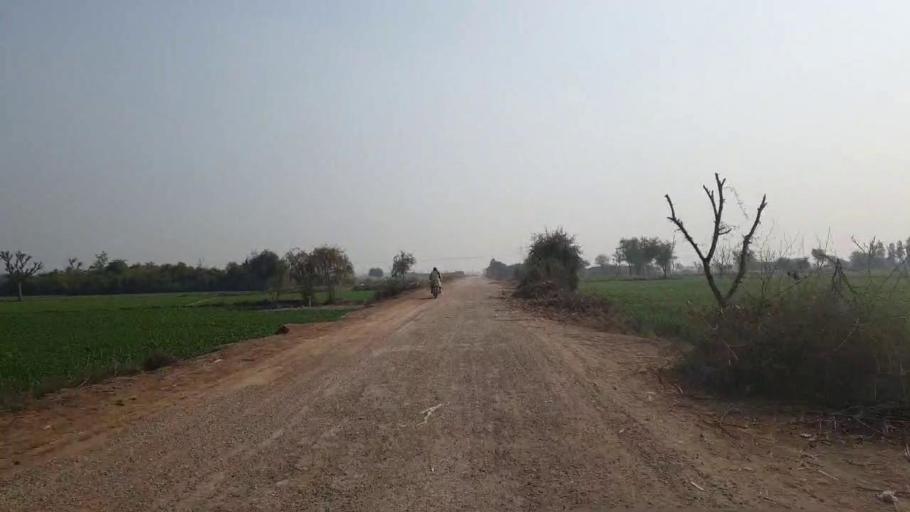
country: PK
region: Sindh
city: Hala
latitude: 25.9432
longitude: 68.4391
